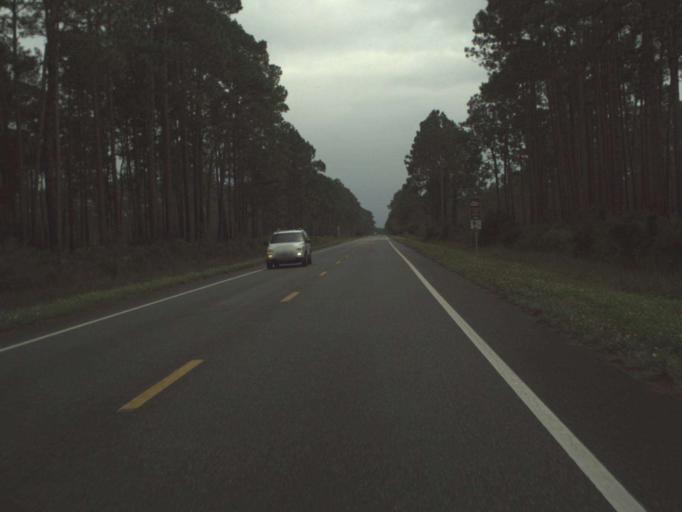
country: US
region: Florida
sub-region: Franklin County
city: Eastpoint
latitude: 29.8158
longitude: -84.8465
